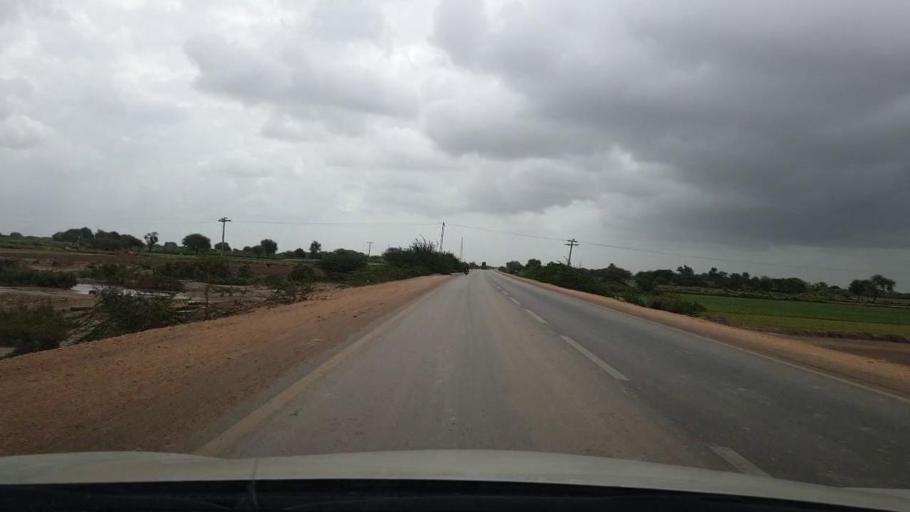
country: PK
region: Sindh
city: Mirpur Batoro
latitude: 24.6440
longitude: 68.4184
